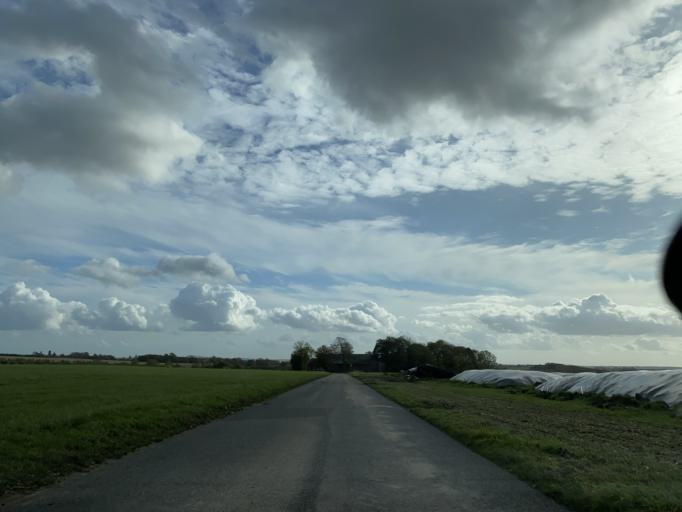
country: DK
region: Central Jutland
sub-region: Arhus Kommune
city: Sabro
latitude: 56.1957
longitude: 10.0022
